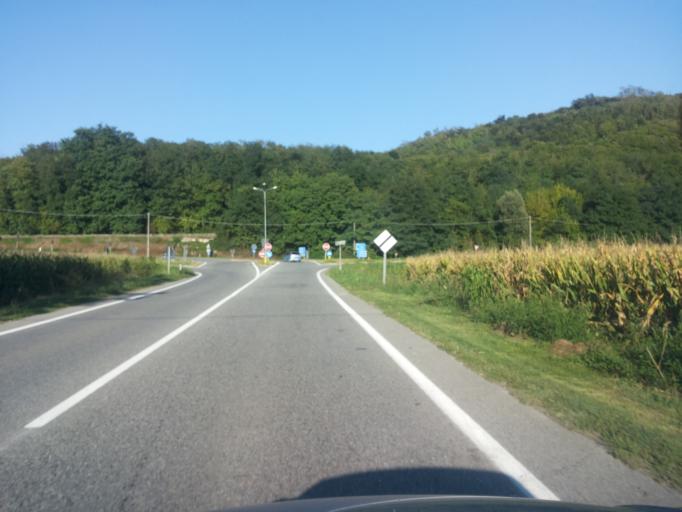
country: IT
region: Piedmont
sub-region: Provincia di Torino
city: Vestigne
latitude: 45.3971
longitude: 7.9417
